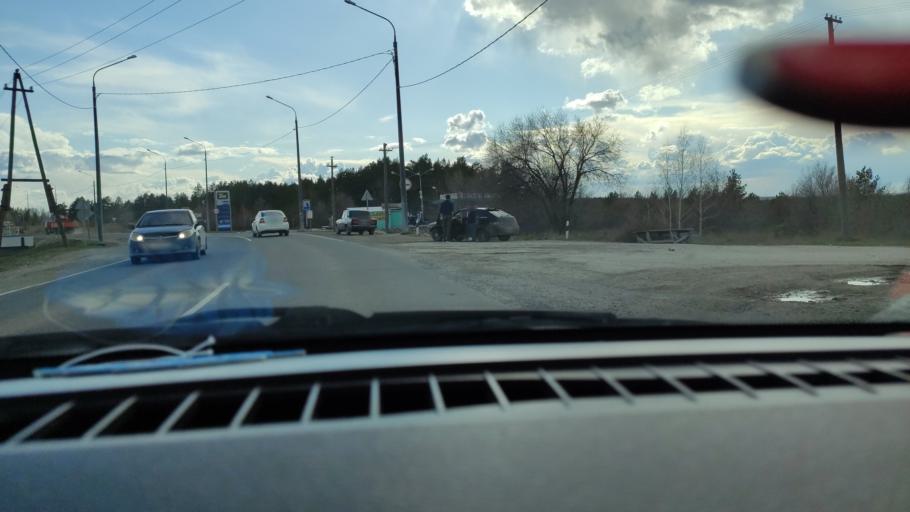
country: RU
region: Saratov
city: Sennoy
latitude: 52.1487
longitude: 46.9472
